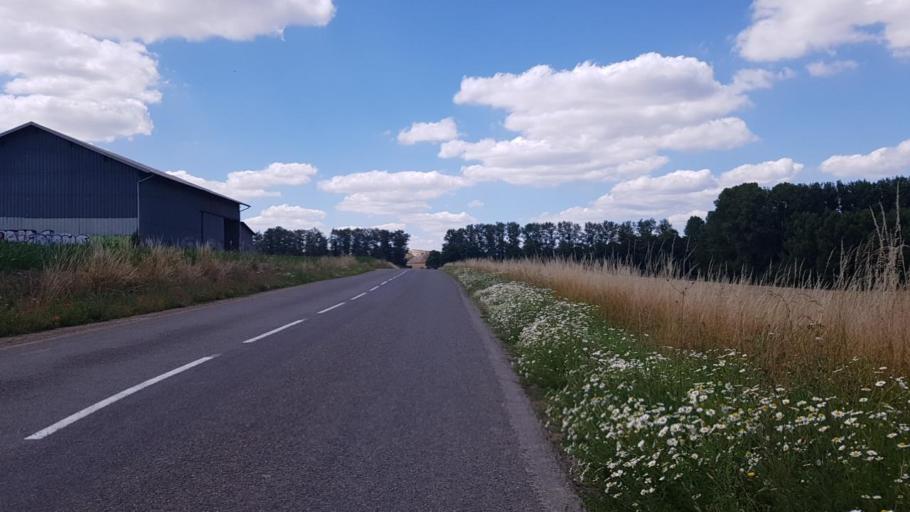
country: FR
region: Ile-de-France
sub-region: Departement de Seine-et-Marne
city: Longperrier
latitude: 49.0161
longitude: 2.6538
